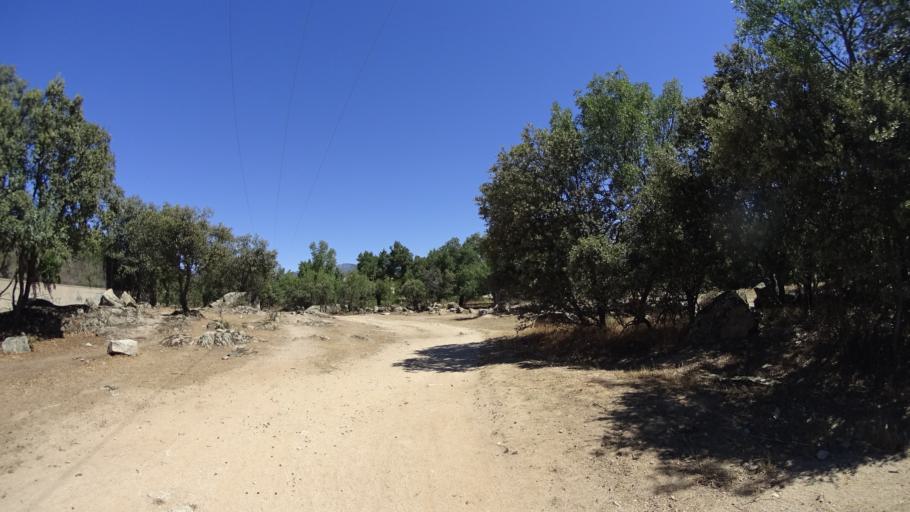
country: ES
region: Madrid
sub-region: Provincia de Madrid
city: Alpedrete
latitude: 40.6604
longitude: -4.0479
